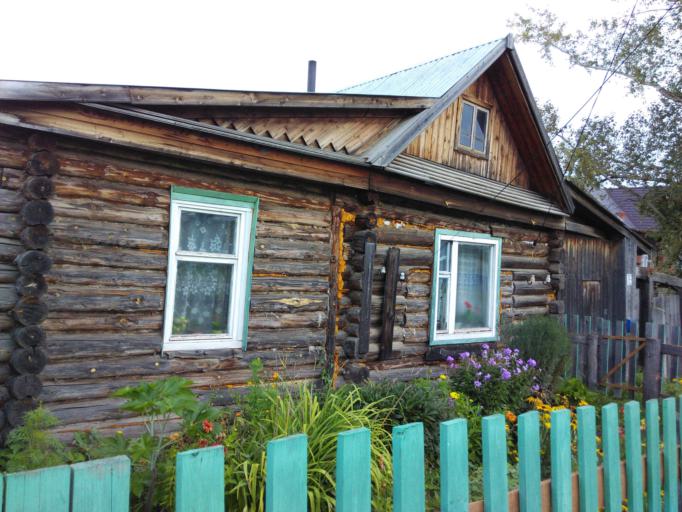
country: RU
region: Perm
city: Foki
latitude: 56.6952
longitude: 54.3511
